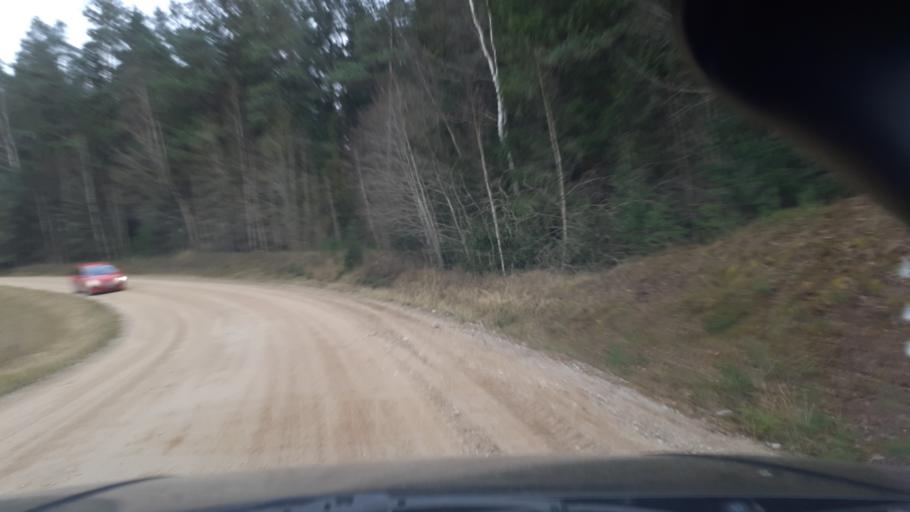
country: LV
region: Alsunga
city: Alsunga
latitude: 56.9849
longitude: 21.6705
